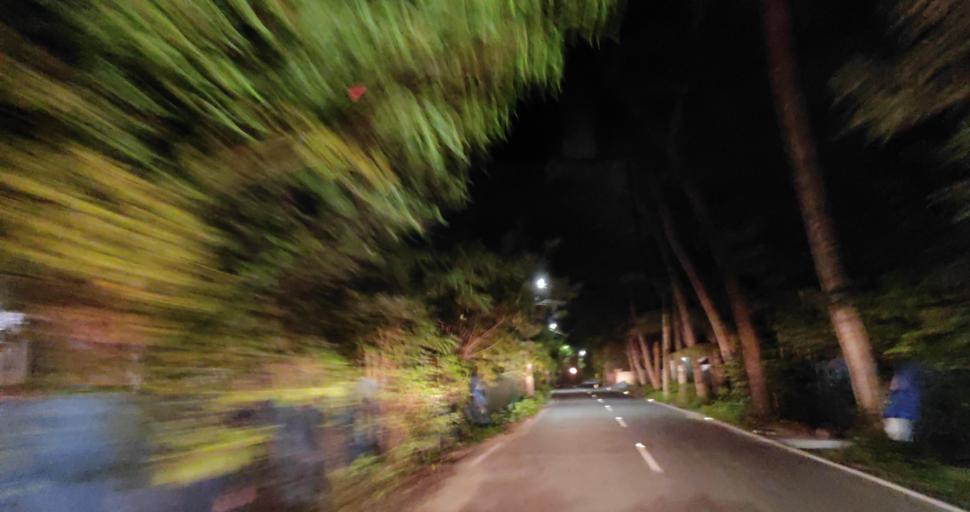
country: IN
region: Kerala
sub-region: Alappuzha
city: Vayalar
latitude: 9.7462
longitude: 76.2870
